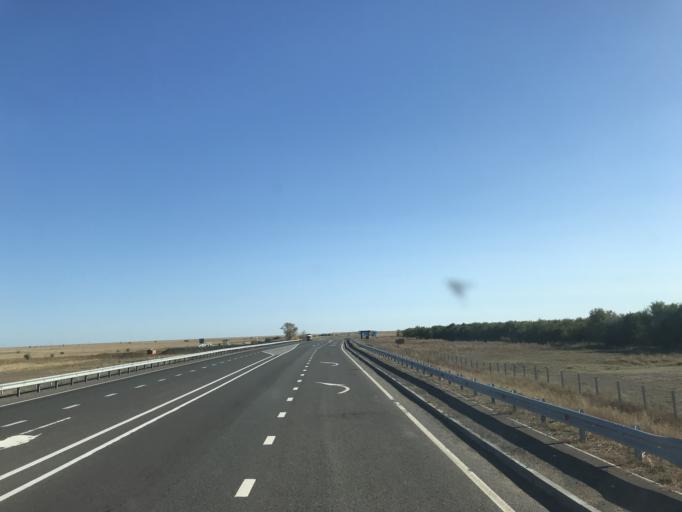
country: KZ
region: Pavlodar
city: Aksu
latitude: 52.0173
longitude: 77.2341
